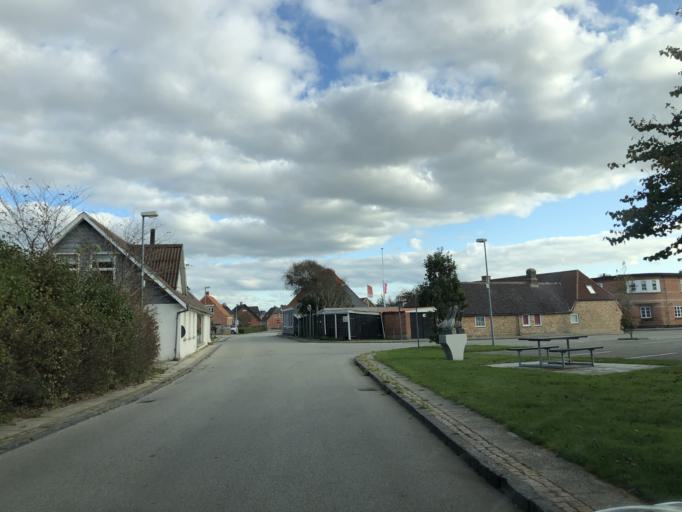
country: DK
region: Central Jutland
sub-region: Holstebro Kommune
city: Ulfborg
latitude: 56.3068
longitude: 8.1852
